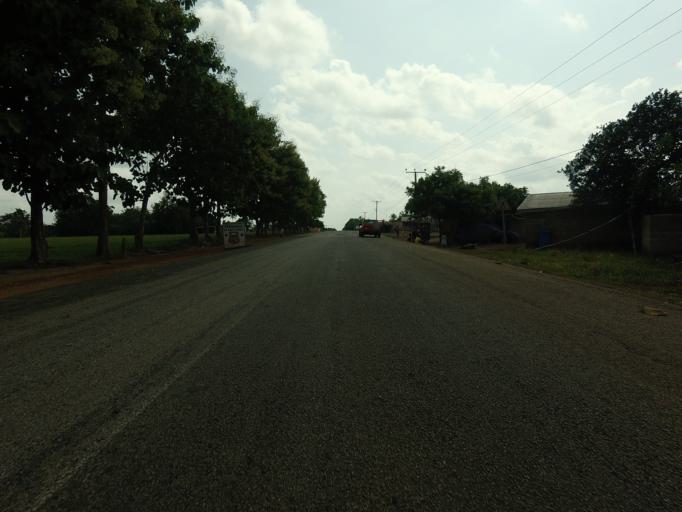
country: TG
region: Maritime
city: Tsevie
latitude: 6.3920
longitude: 0.8356
